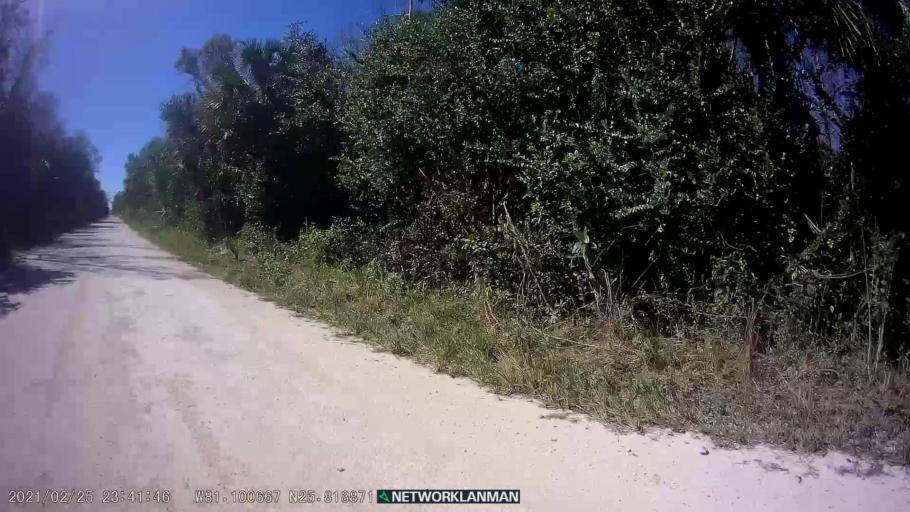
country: US
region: Florida
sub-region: Collier County
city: Marco
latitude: 25.8137
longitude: -81.1007
